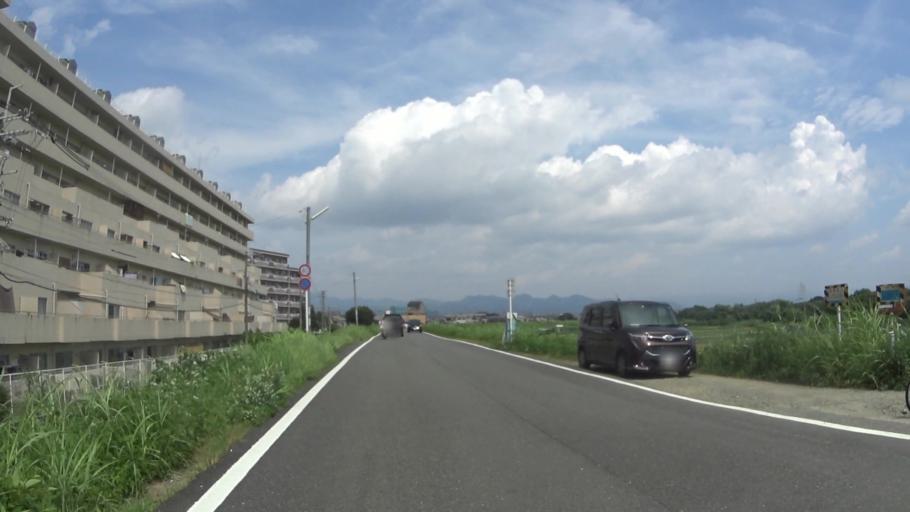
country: JP
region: Kyoto
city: Muko
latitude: 34.9661
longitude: 135.7199
